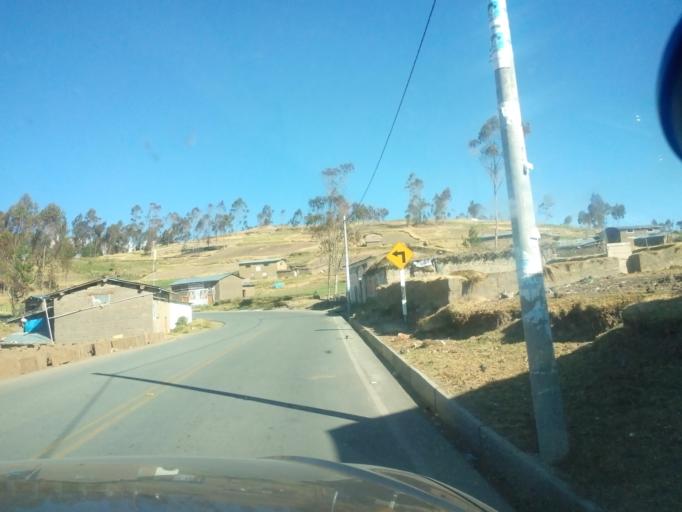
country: PE
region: Apurimac
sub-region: Provincia de Andahuaylas
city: Pacucha
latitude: -13.6506
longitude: -73.2971
